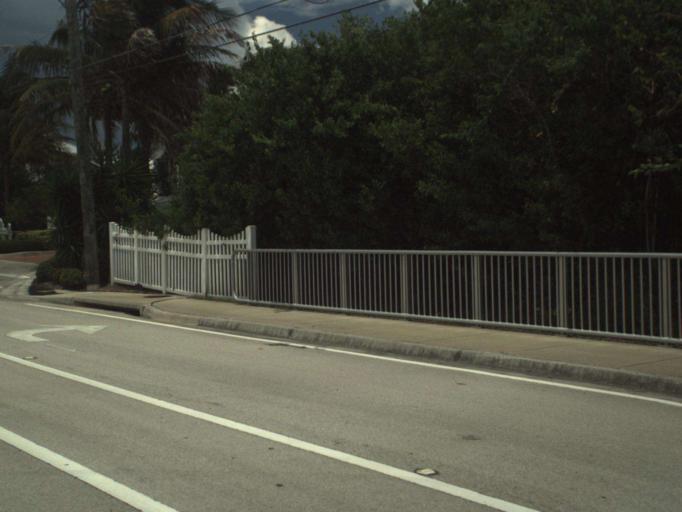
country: US
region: Florida
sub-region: Saint Lucie County
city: Indian River Estates
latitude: 27.3880
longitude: -80.2600
